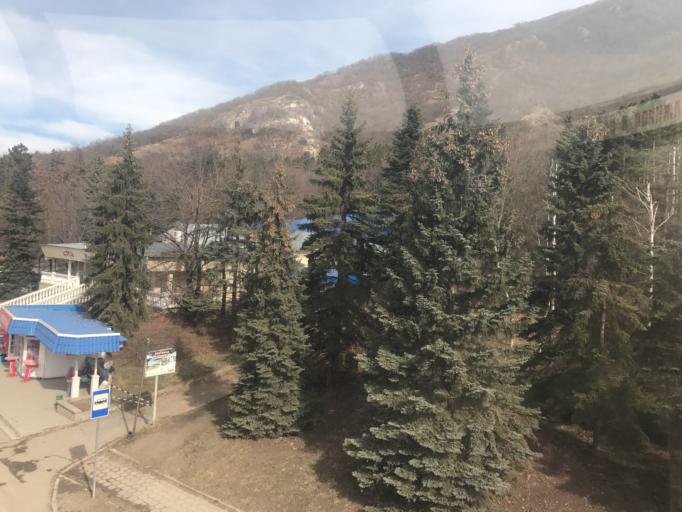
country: RU
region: Stavropol'skiy
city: Pyatigorsk
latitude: 44.0439
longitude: 43.0816
